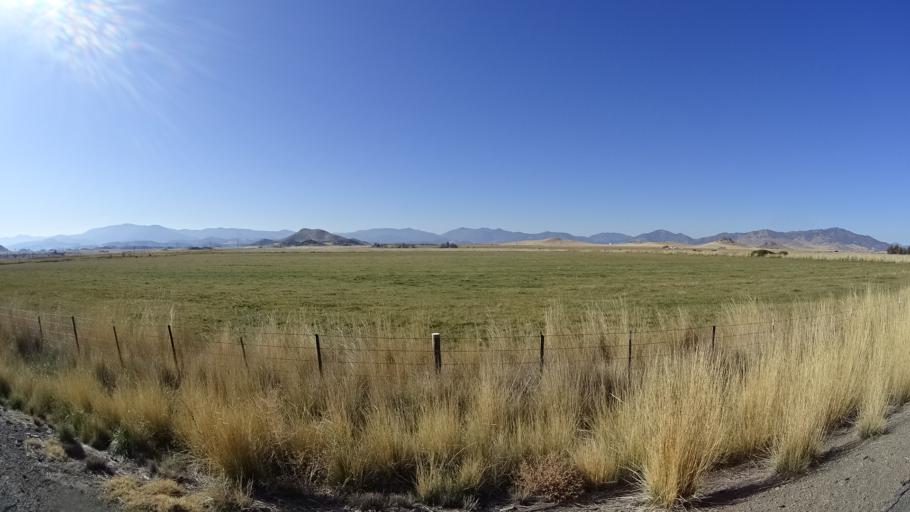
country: US
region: California
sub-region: Siskiyou County
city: Montague
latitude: 41.7293
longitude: -122.4574
